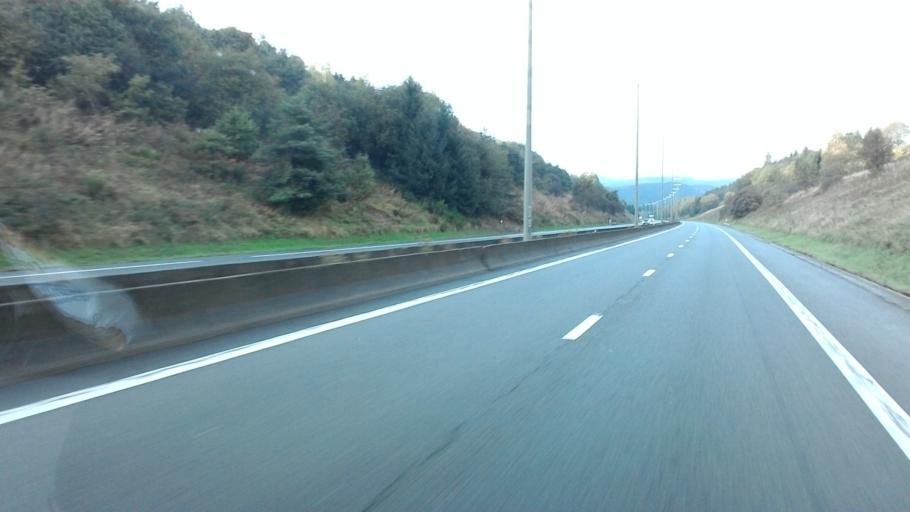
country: BE
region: Wallonia
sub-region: Province du Luxembourg
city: Manhay
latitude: 50.2789
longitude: 5.7280
